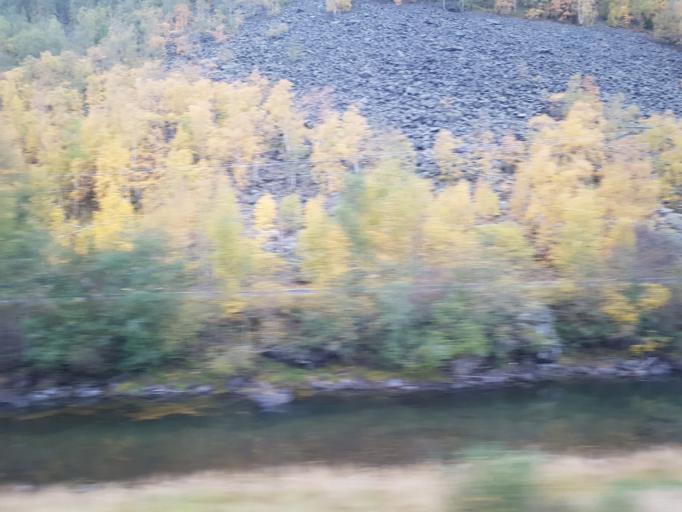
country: NO
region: Oppland
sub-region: Sel
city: Otta
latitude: 61.8036
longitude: 9.5498
